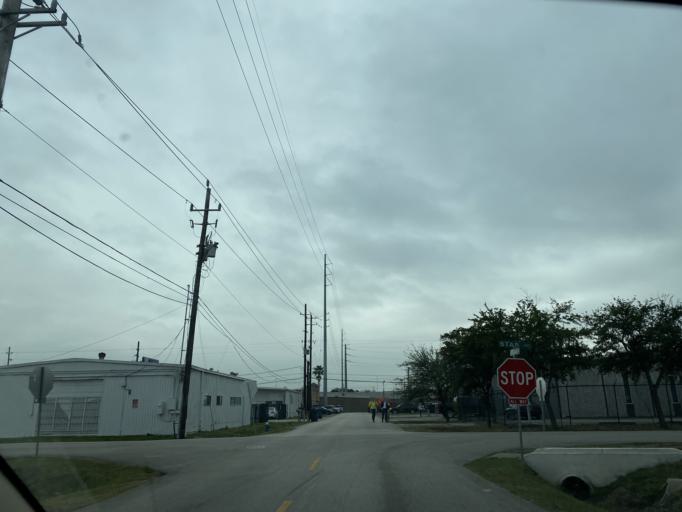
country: US
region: Texas
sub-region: Harris County
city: Bellaire
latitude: 29.7277
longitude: -95.4803
